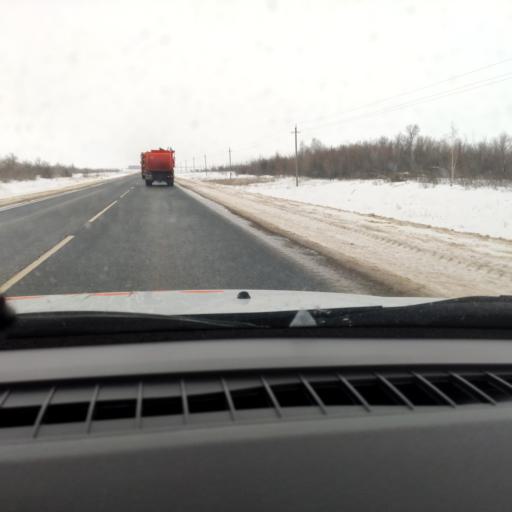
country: RU
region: Saratov
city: Perelyub
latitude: 52.1668
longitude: 50.7971
